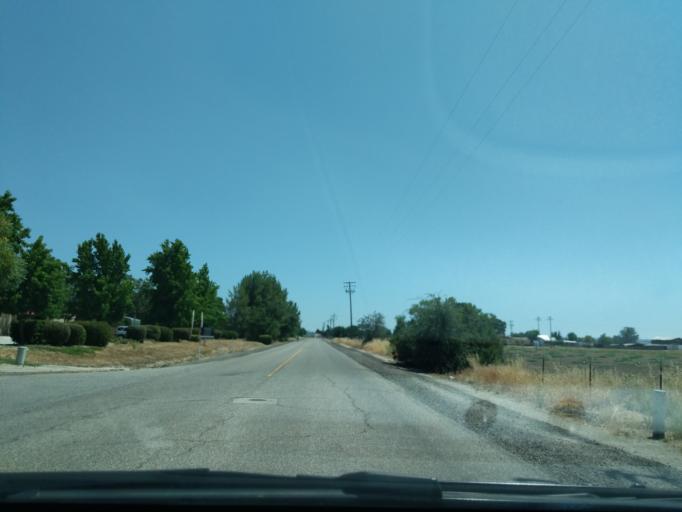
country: US
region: California
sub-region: San Luis Obispo County
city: Paso Robles
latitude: 35.6757
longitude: -120.6409
